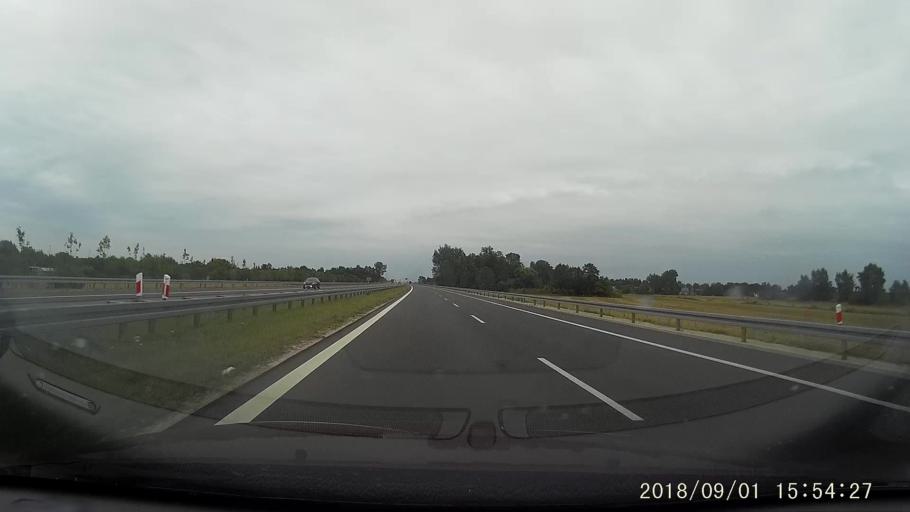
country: PL
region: Lubusz
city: Gorzow Wielkopolski
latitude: 52.7003
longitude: 15.2157
